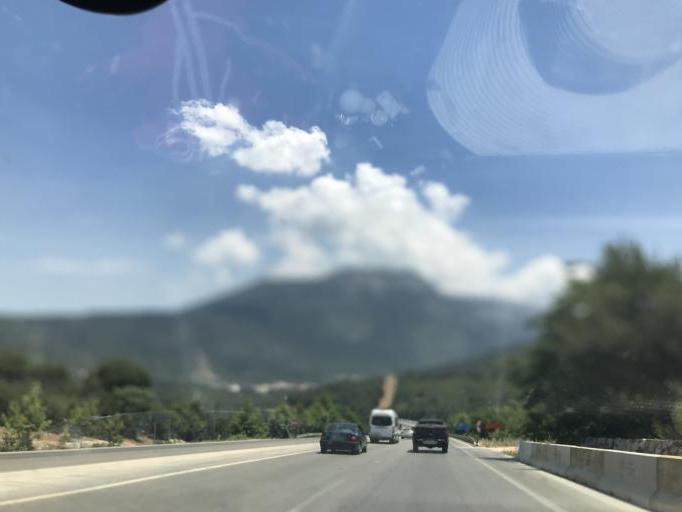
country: TR
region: Denizli
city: Honaz
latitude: 37.7321
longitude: 29.1815
